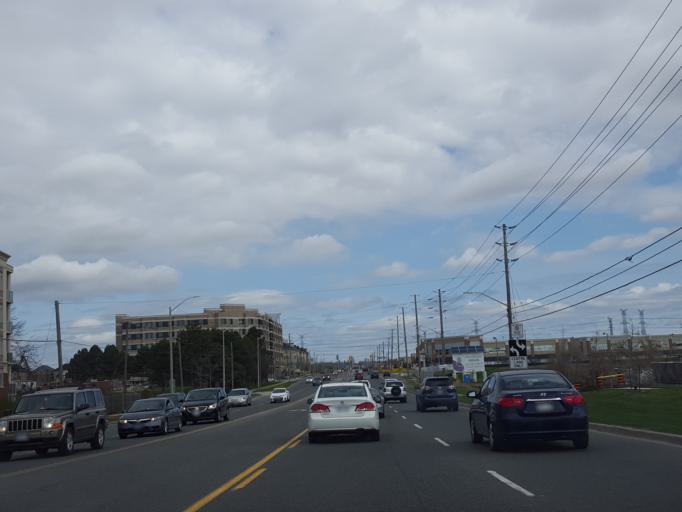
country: CA
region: Ontario
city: Markham
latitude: 43.8455
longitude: -79.2531
